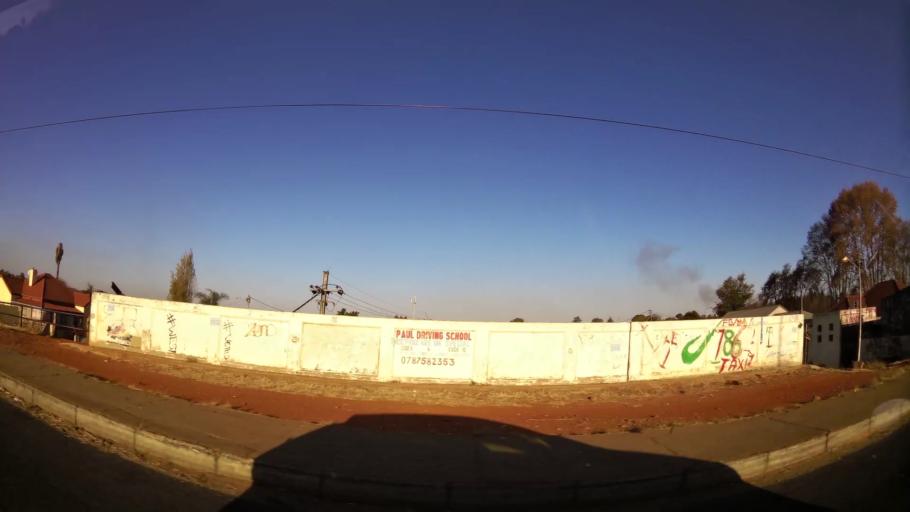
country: ZA
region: Gauteng
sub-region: City of Johannesburg Metropolitan Municipality
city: Roodepoort
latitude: -26.1628
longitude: 27.8723
